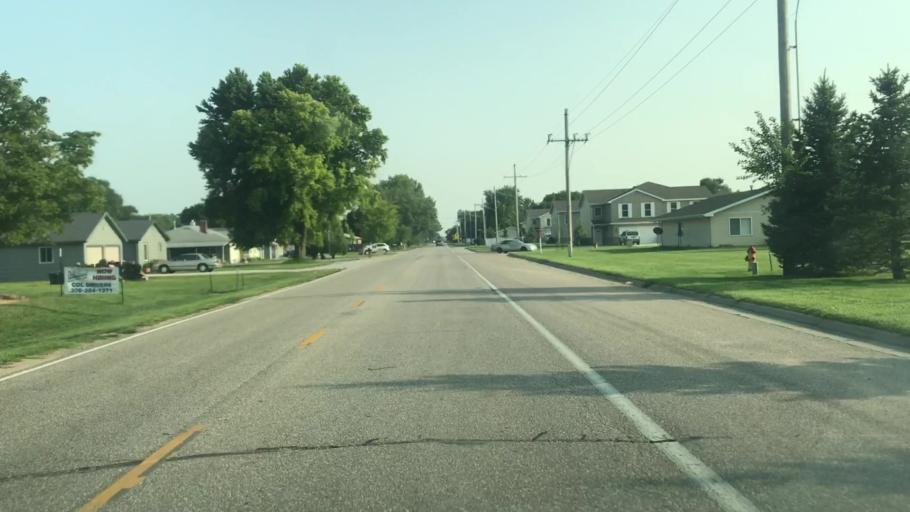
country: US
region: Nebraska
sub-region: Hall County
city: Grand Island
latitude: 40.9335
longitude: -98.3015
